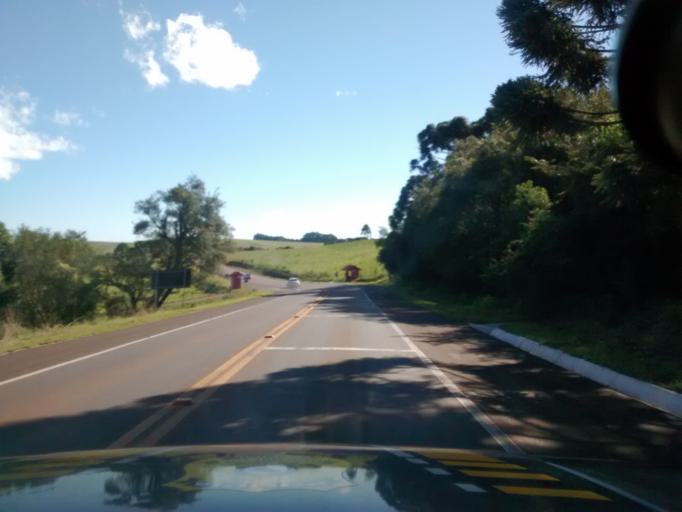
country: BR
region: Rio Grande do Sul
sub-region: Lagoa Vermelha
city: Lagoa Vermelha
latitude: -28.3209
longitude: -51.2222
